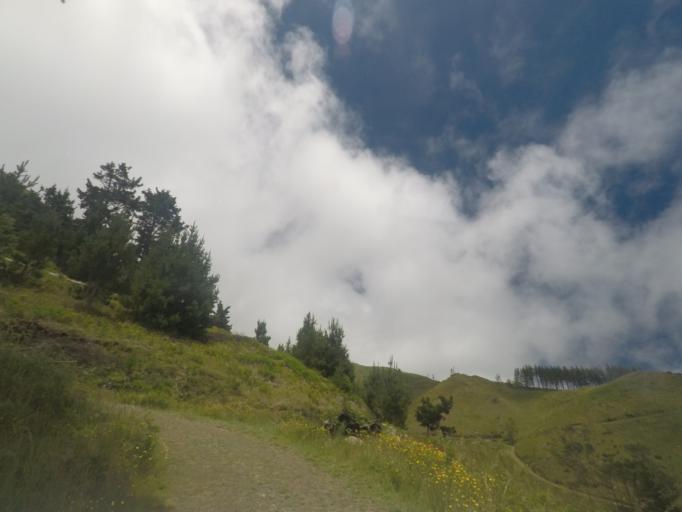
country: PT
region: Madeira
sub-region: Funchal
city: Nossa Senhora do Monte
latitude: 32.7014
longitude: -16.9053
